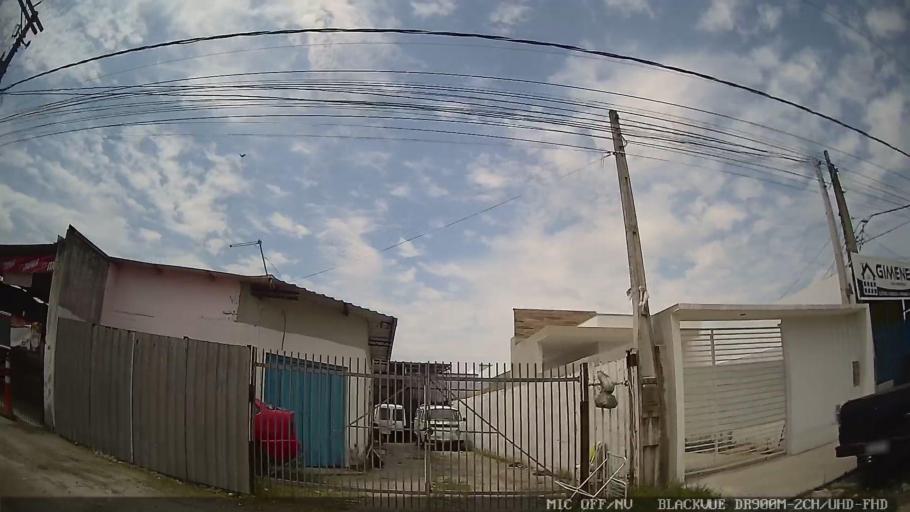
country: BR
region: Sao Paulo
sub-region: Caraguatatuba
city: Caraguatatuba
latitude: -23.6688
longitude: -45.4549
